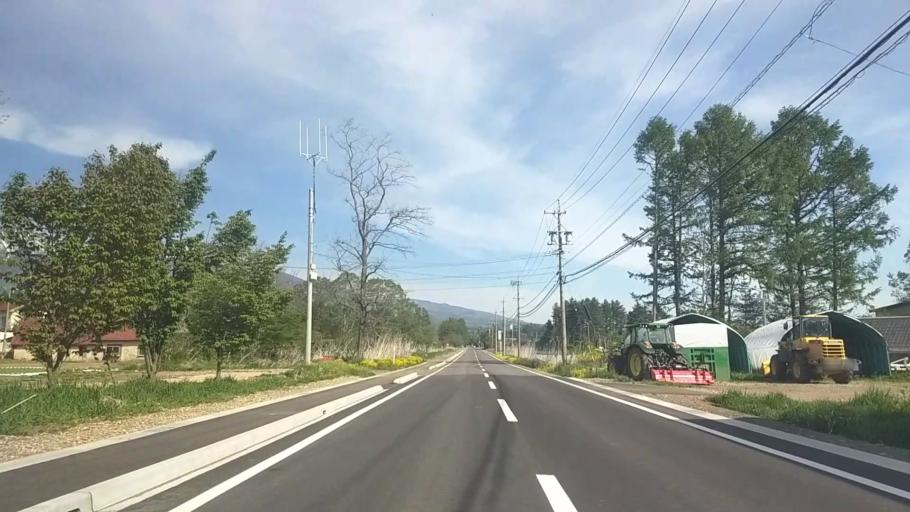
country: JP
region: Yamanashi
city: Nirasaki
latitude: 35.9469
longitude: 138.4777
